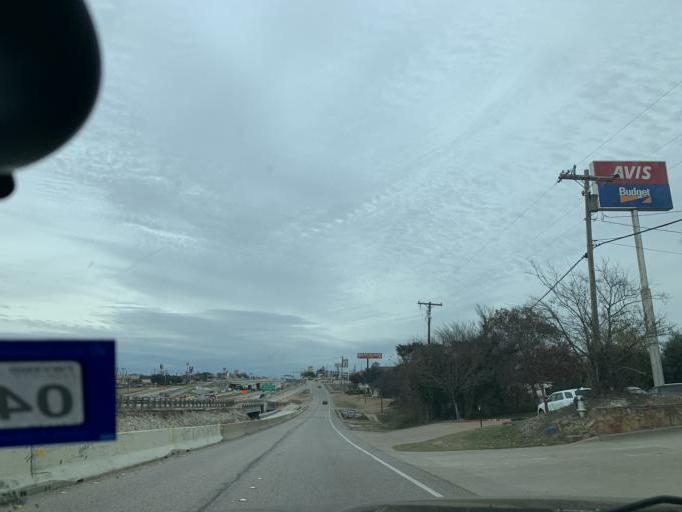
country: US
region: Texas
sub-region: Dallas County
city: Duncanville
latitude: 32.6377
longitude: -96.8946
